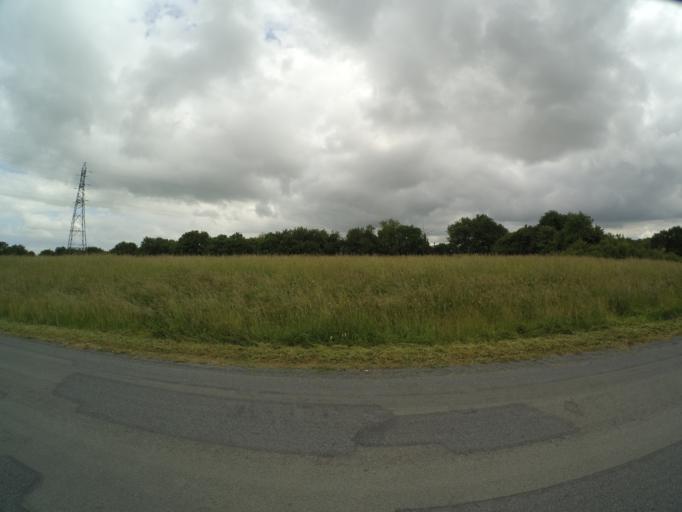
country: FR
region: Poitou-Charentes
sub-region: Departement de la Charente-Maritime
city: Breuil-Magne
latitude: 45.9677
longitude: -0.9766
